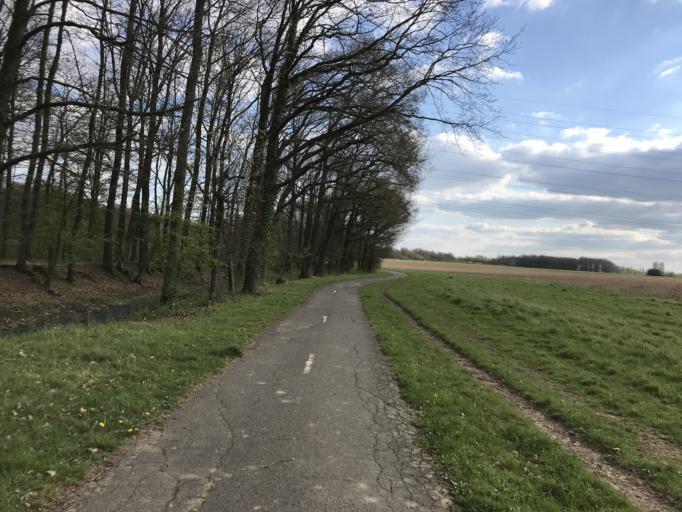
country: FR
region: Ile-de-France
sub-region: Departement de l'Essonne
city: Vauhallan
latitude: 48.7448
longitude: 2.2091
